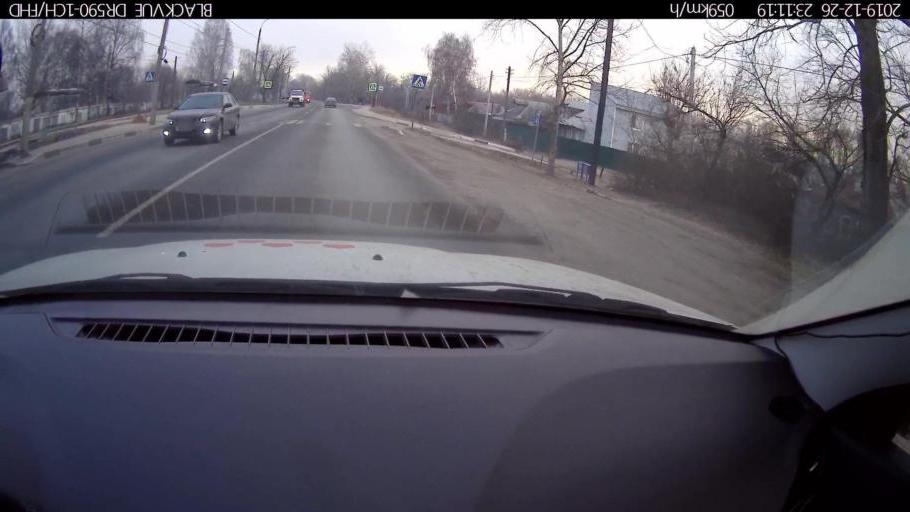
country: RU
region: Nizjnij Novgorod
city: Burevestnik
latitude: 56.2061
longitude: 43.7958
